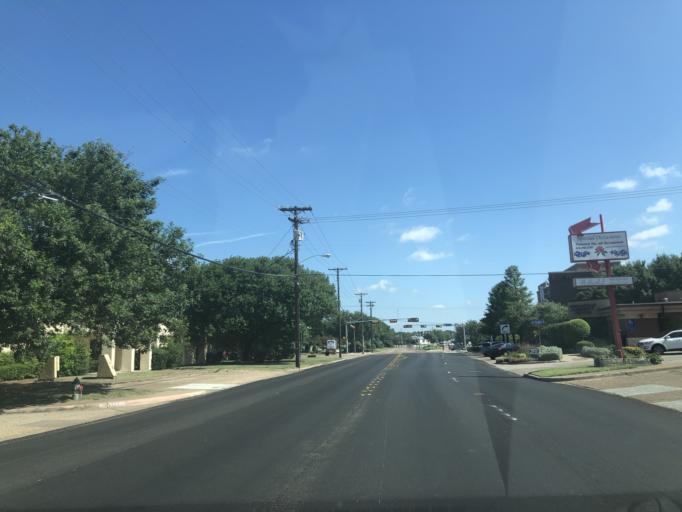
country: US
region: Texas
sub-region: Dallas County
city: Duncanville
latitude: 32.6506
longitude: -96.9085
